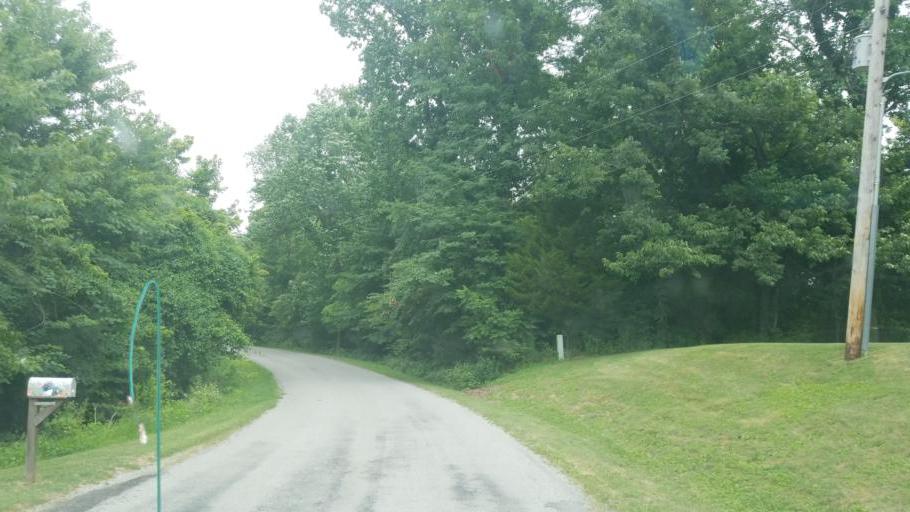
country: US
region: Illinois
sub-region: Jackson County
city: Murphysboro
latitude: 37.6721
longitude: -89.3899
